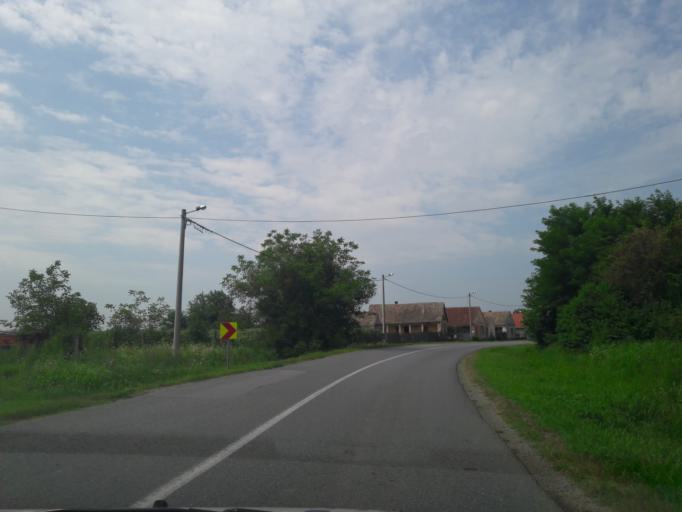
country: HR
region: Osjecko-Baranjska
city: Vuka
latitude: 45.5031
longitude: 18.4497
